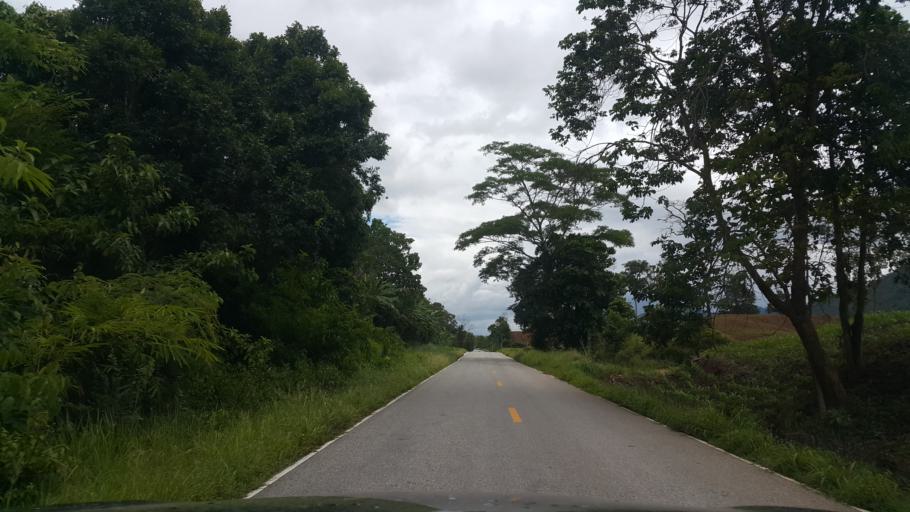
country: TH
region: Phitsanulok
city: Chat Trakan
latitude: 17.3618
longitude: 100.7364
